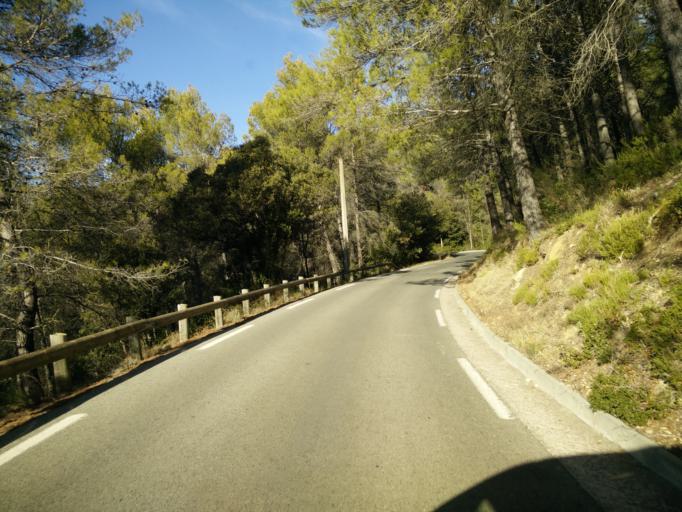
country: FR
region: Provence-Alpes-Cote d'Azur
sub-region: Departement du Var
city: Taradeau
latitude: 43.4551
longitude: 6.4333
